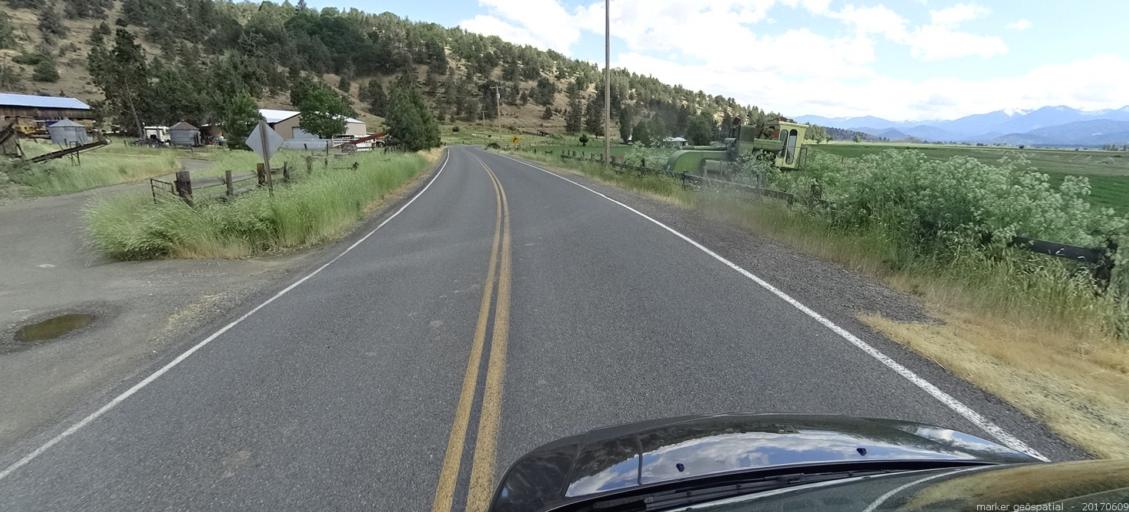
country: US
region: California
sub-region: Siskiyou County
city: Yreka
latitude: 41.5179
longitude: -122.8408
